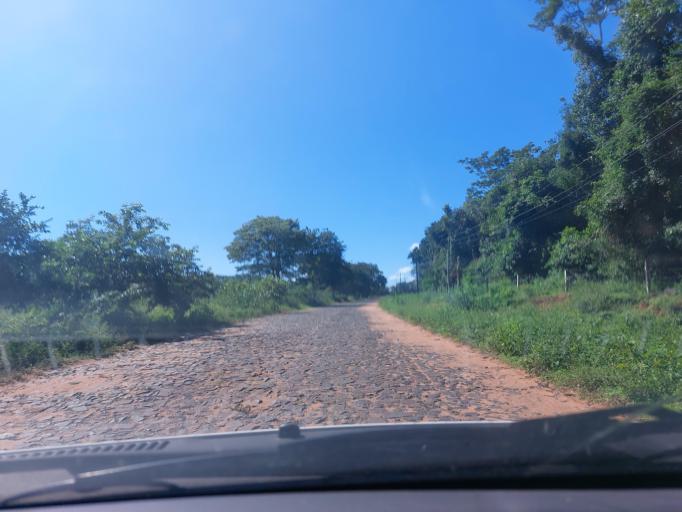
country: PY
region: San Pedro
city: Itacurubi del Rosario
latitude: -24.5778
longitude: -56.6001
